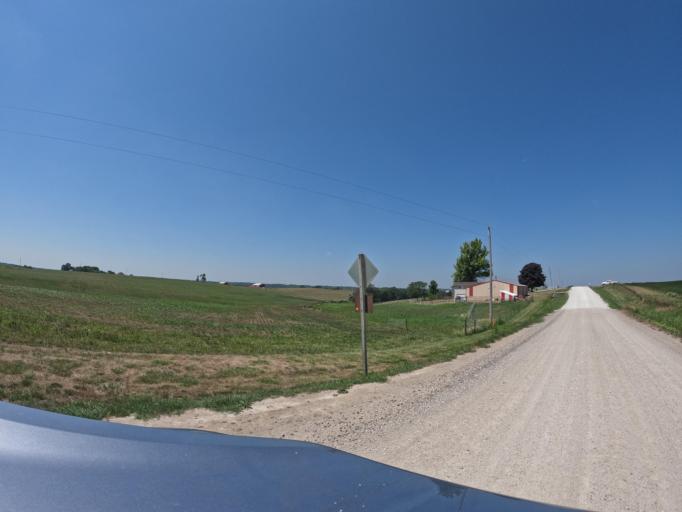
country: US
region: Iowa
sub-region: Keokuk County
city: Sigourney
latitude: 41.2505
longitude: -92.2076
